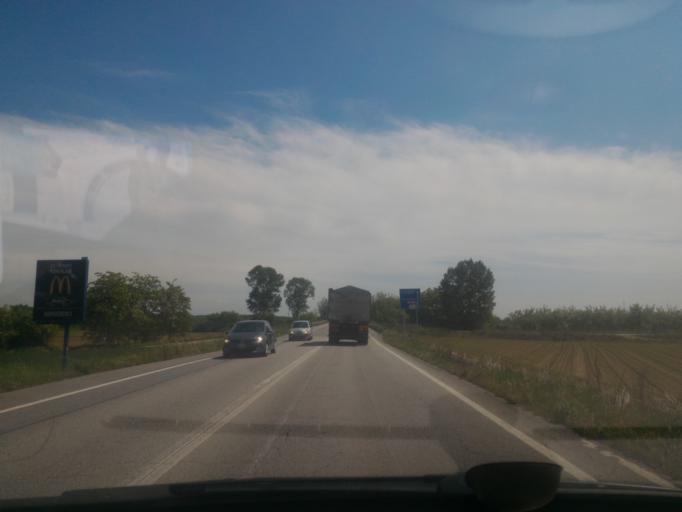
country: IT
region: Piedmont
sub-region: Provincia di Torino
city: Trofarello
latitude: 44.9583
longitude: 7.7119
